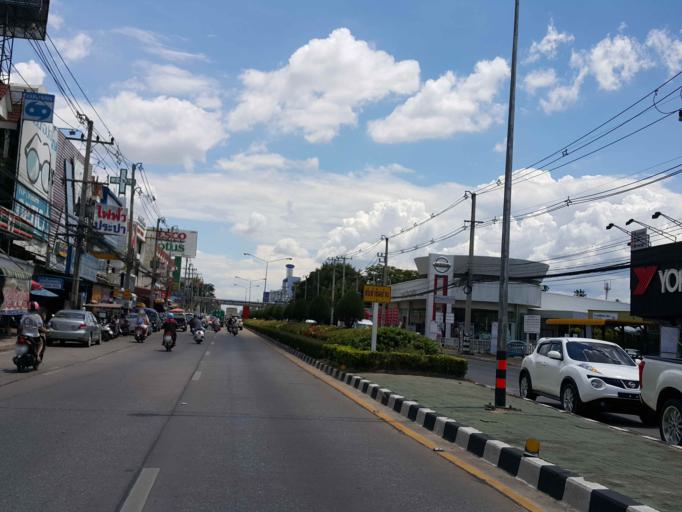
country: TH
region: Chiang Mai
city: Chiang Mai
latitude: 18.7615
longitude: 98.9723
